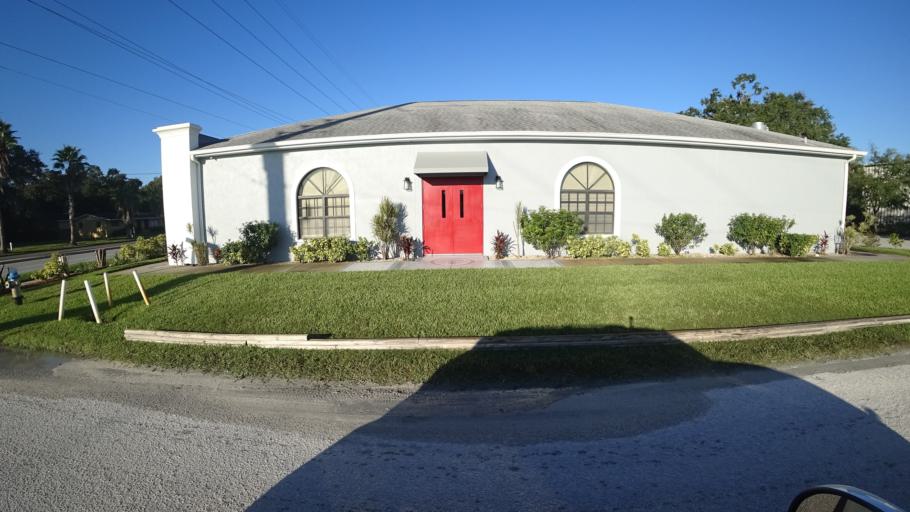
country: US
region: Florida
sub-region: Manatee County
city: Bradenton
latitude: 27.4919
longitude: -82.5578
